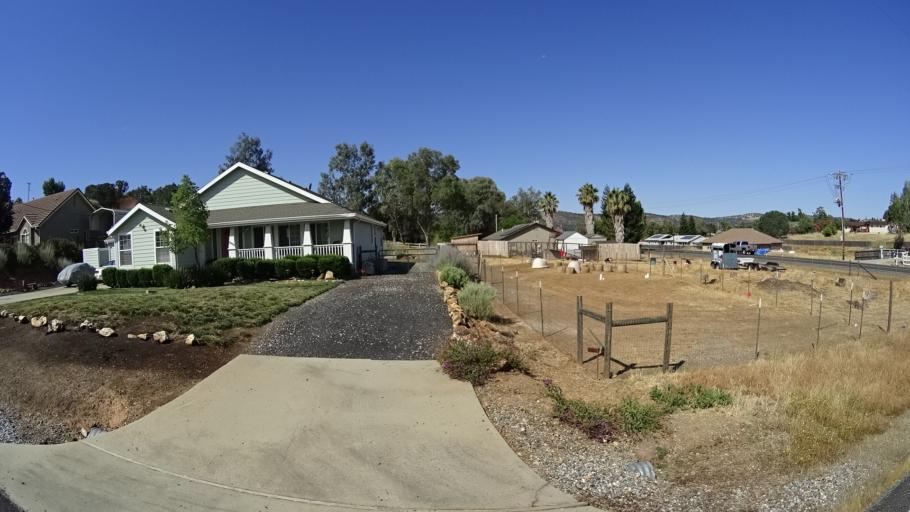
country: US
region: California
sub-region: Calaveras County
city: Copperopolis
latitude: 37.9344
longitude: -120.6379
